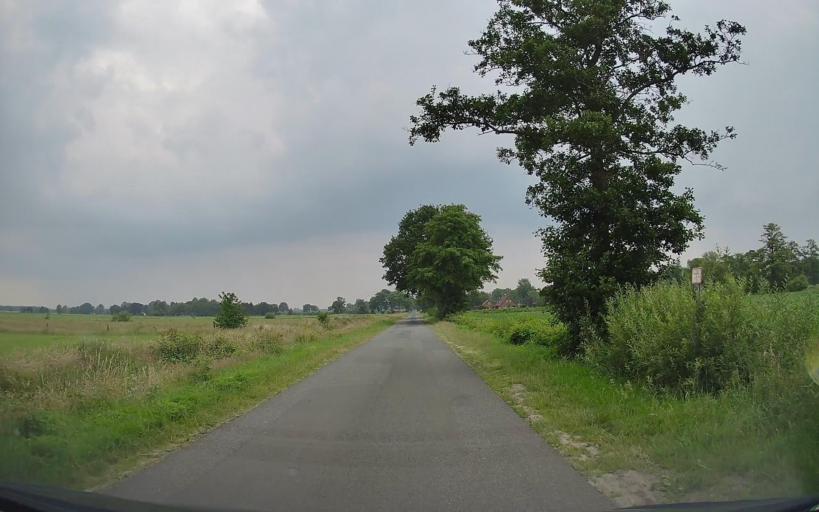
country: DE
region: Lower Saxony
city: Friesoythe
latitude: 53.0434
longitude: 7.8472
